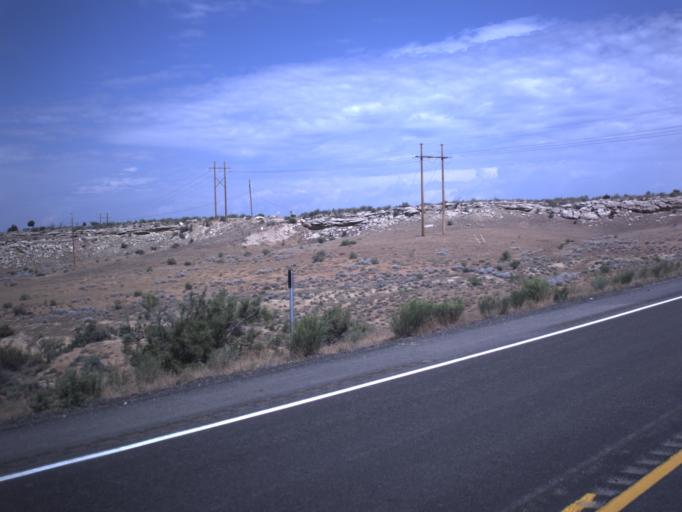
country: US
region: Utah
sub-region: Uintah County
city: Naples
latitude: 40.1901
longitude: -109.3309
